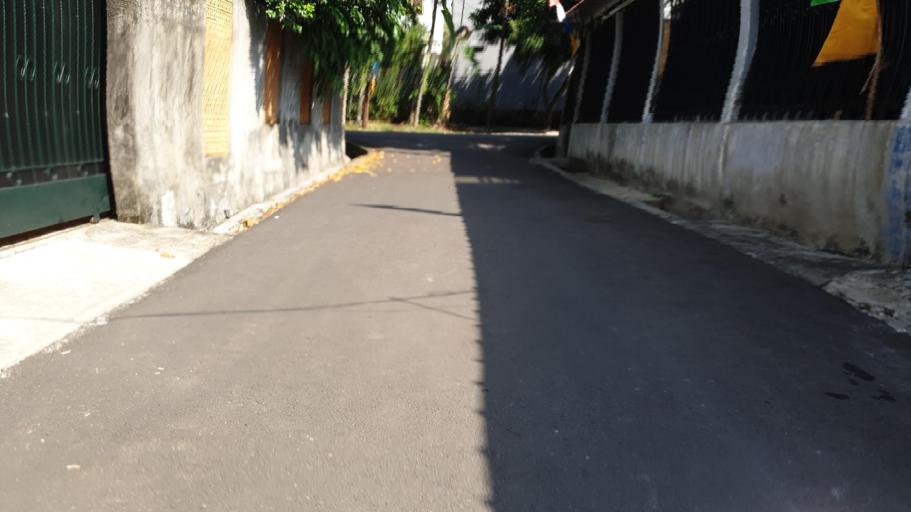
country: ID
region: Jakarta Raya
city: Jakarta
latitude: -6.2938
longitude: 106.8389
